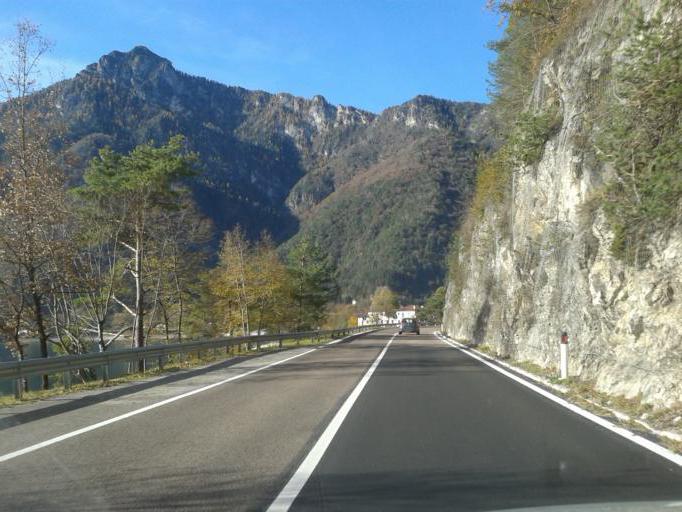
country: IT
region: Trentino-Alto Adige
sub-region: Provincia di Trento
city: Pieve di Ledro
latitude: 45.8861
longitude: 10.7395
